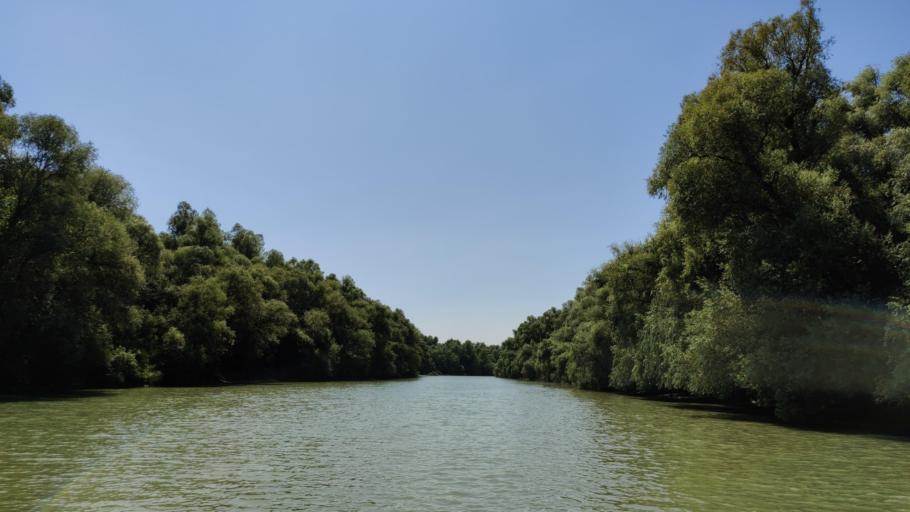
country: RO
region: Tulcea
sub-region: Comuna Pardina
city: Pardina
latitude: 45.2397
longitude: 28.9188
